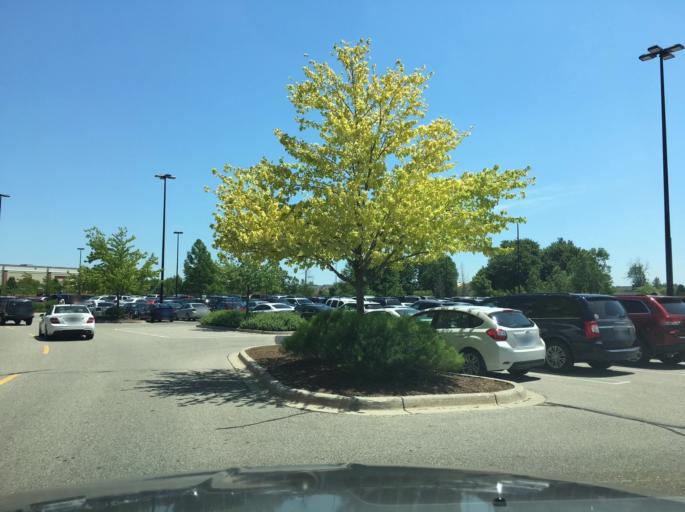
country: US
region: Michigan
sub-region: Macomb County
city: Clinton
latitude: 42.6249
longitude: -82.9488
